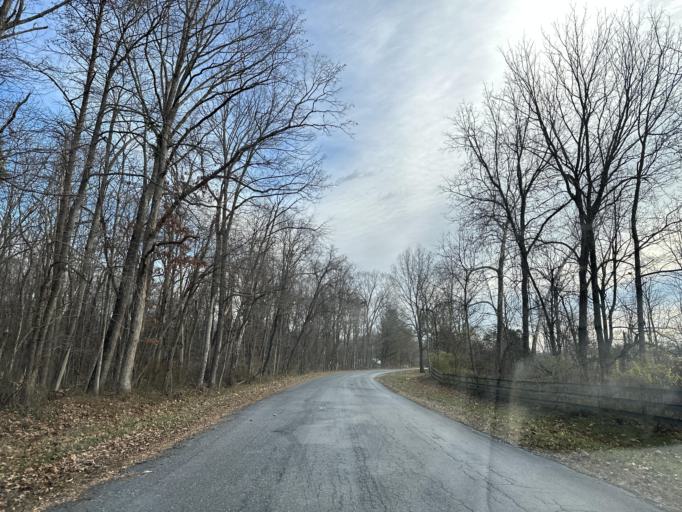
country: US
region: Virginia
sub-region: City of Staunton
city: Staunton
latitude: 38.2125
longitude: -79.2261
